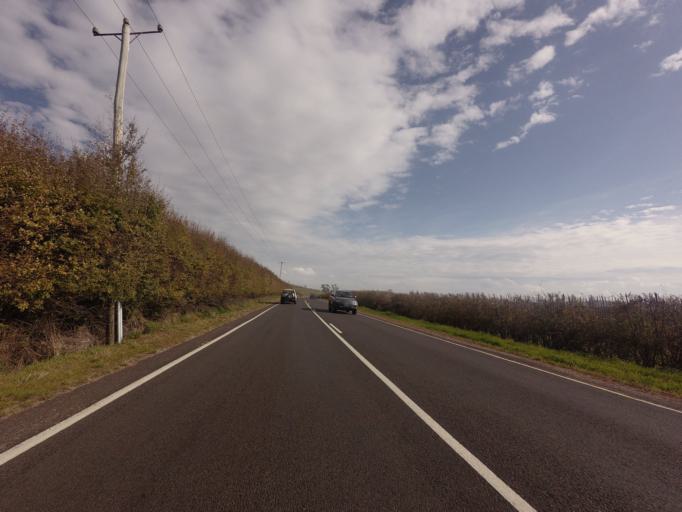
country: AU
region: Tasmania
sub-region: Meander Valley
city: Westbury
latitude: -41.5259
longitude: 146.7662
